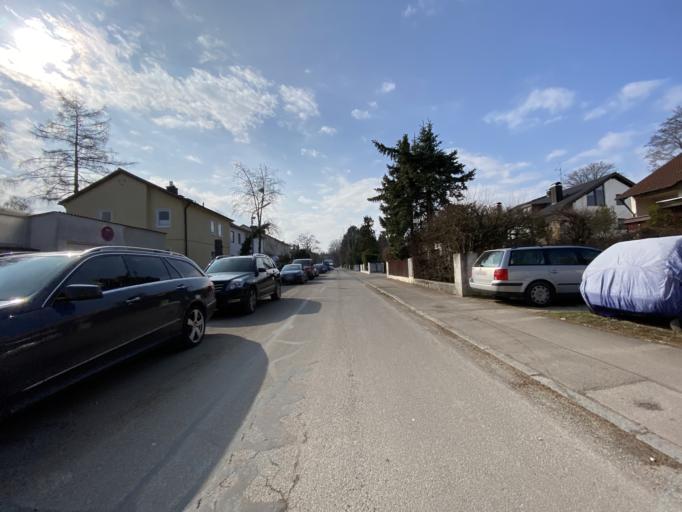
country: DE
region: Bavaria
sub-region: Upper Bavaria
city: Bogenhausen
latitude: 48.1533
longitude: 11.6402
